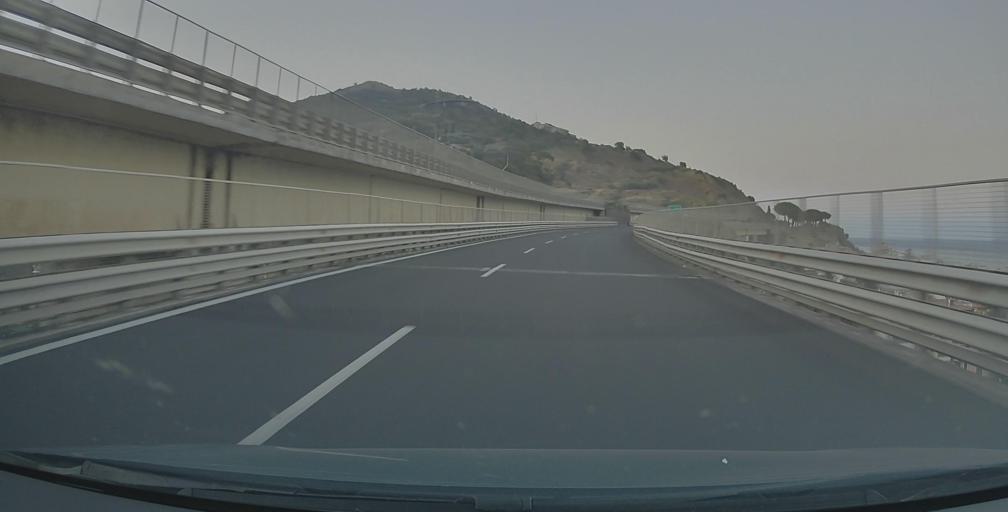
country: IT
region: Sicily
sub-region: Messina
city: Letojanni
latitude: 37.8797
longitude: 15.3032
